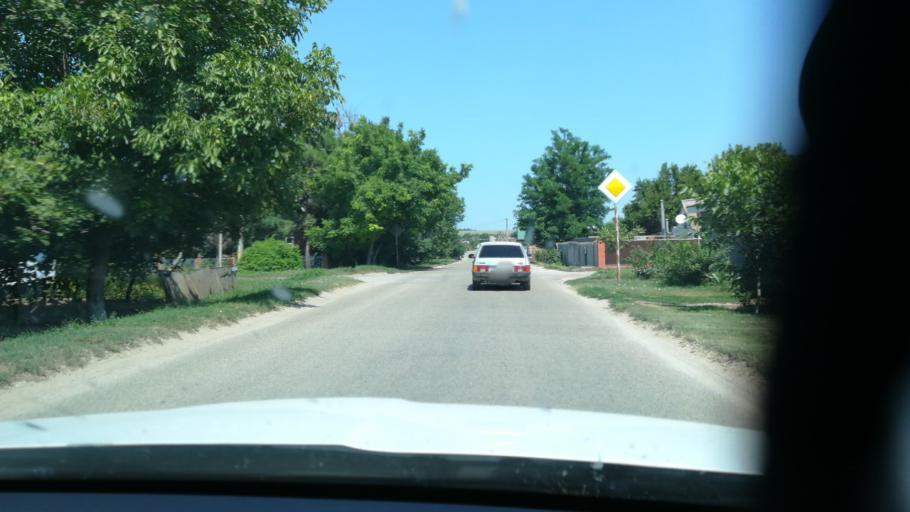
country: RU
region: Krasnodarskiy
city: Starotitarovskaya
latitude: 45.2084
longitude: 37.1459
